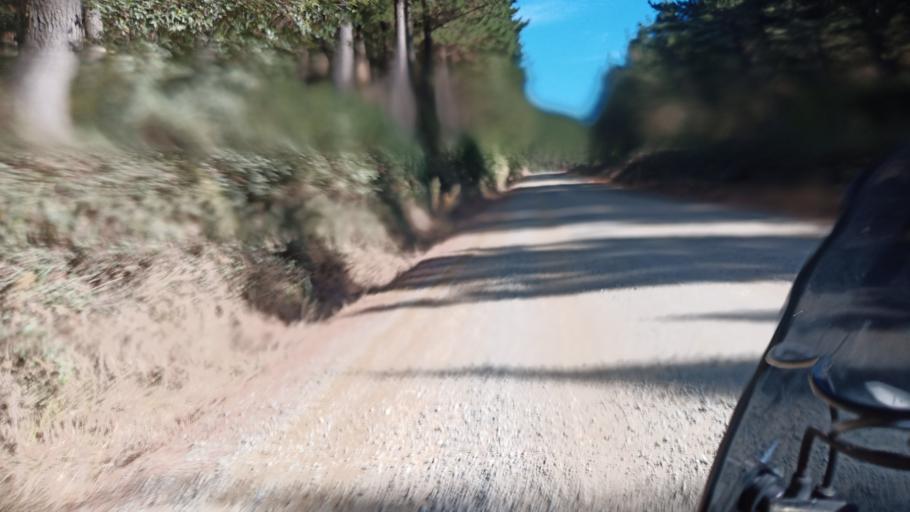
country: NZ
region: Hawke's Bay
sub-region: Wairoa District
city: Wairoa
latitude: -38.9238
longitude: 177.2092
